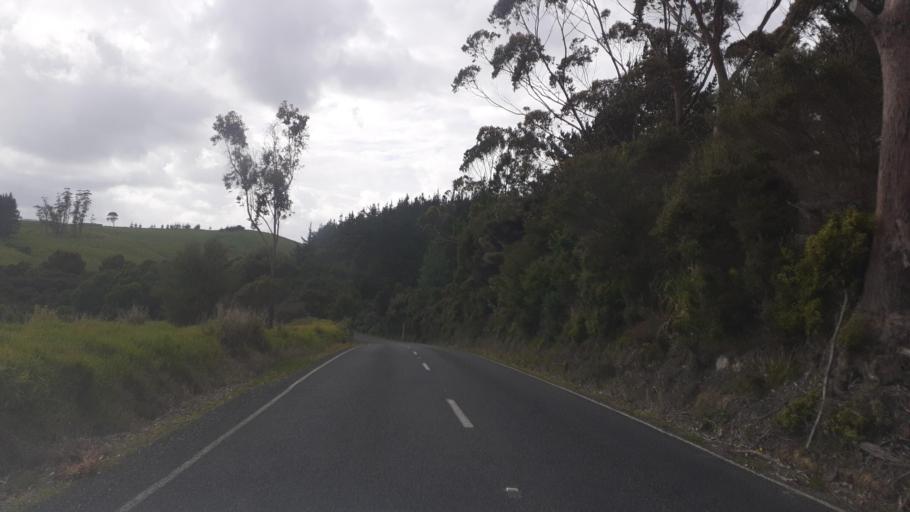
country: NZ
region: Northland
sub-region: Far North District
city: Kerikeri
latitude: -35.2174
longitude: 173.9914
